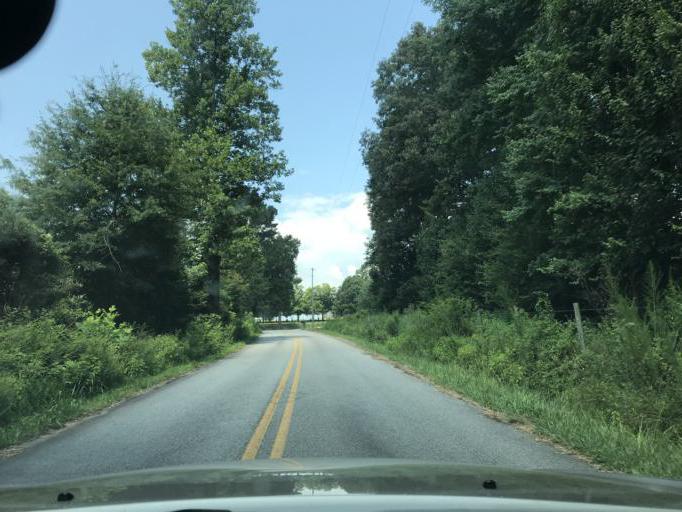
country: US
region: Georgia
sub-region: Dawson County
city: Dawsonville
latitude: 34.3332
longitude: -84.0740
